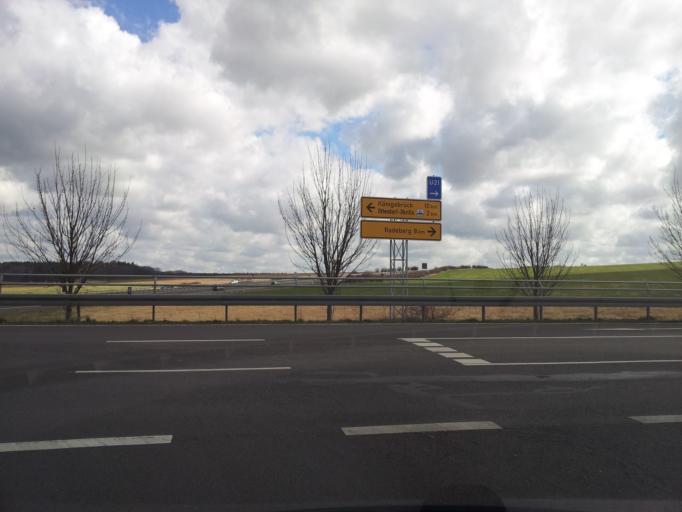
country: DE
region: Saxony
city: Ottendorf-Okrilla
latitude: 51.1708
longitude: 13.8584
